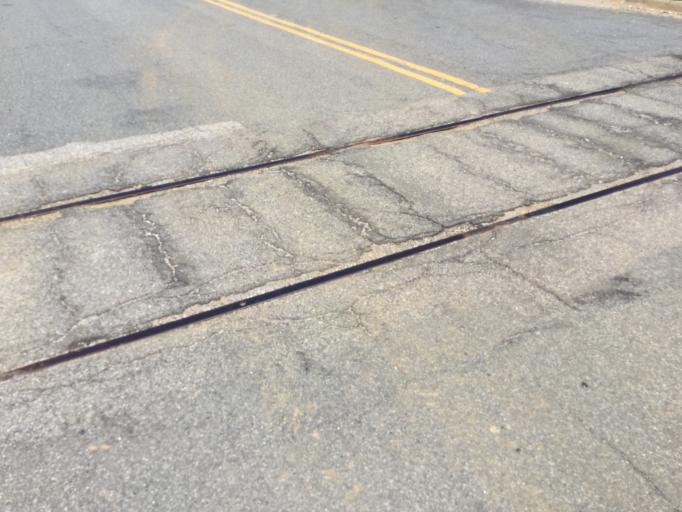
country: US
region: Kansas
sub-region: Johnson County
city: Lenexa
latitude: 38.9300
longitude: -94.7694
